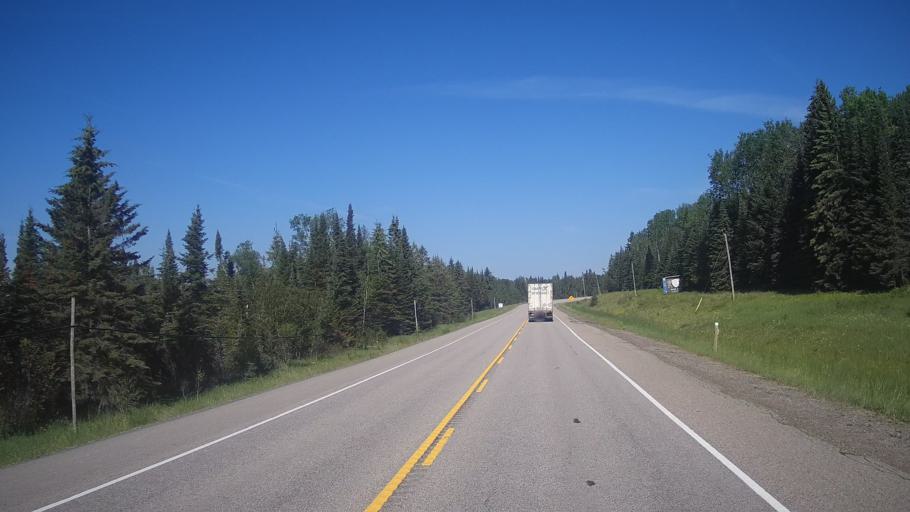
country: CA
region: Ontario
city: Dryden
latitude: 49.6935
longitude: -92.5471
